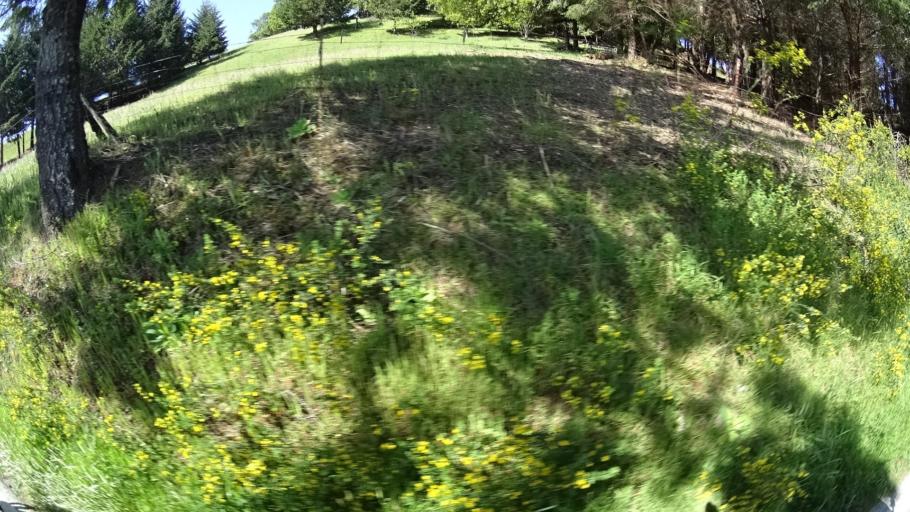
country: US
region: California
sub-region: Humboldt County
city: Redway
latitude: 40.1091
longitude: -123.7512
